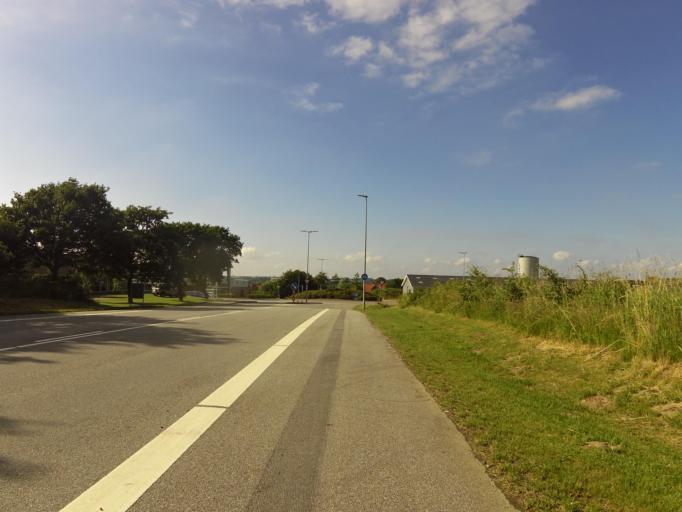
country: DK
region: South Denmark
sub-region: Vejen Kommune
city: Rodding
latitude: 55.3744
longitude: 9.0576
